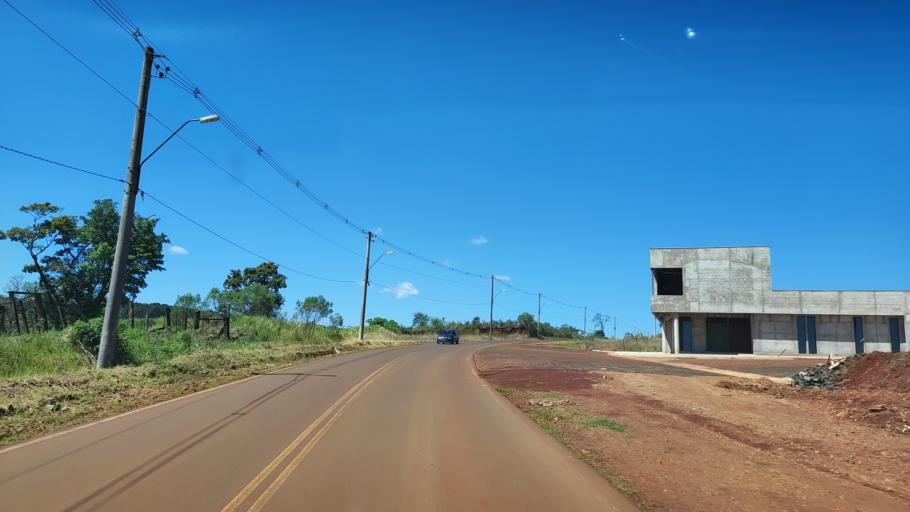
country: AR
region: Misiones
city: Puerto Rico
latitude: -26.8105
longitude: -55.0081
